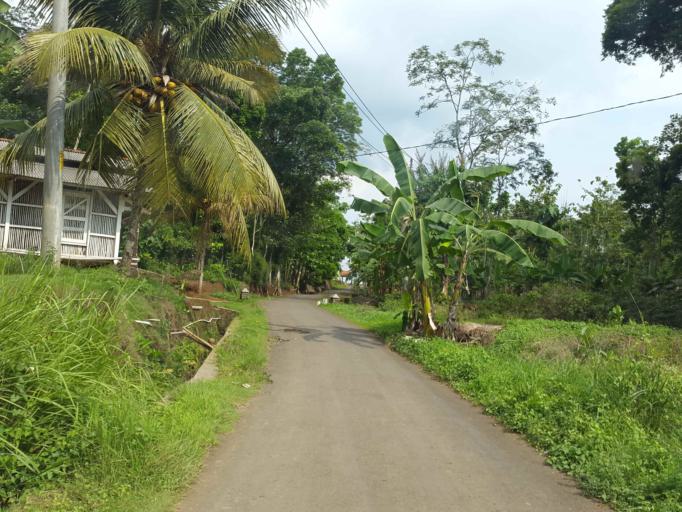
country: ID
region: Central Java
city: Cimalati
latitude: -7.3104
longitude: 108.6522
